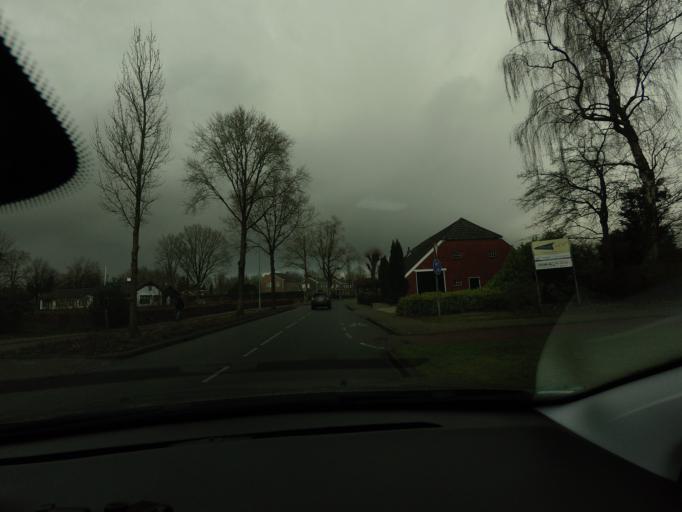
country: NL
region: Drenthe
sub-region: Gemeente Aa en Hunze
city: Anloo
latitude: 53.0029
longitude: 6.7542
